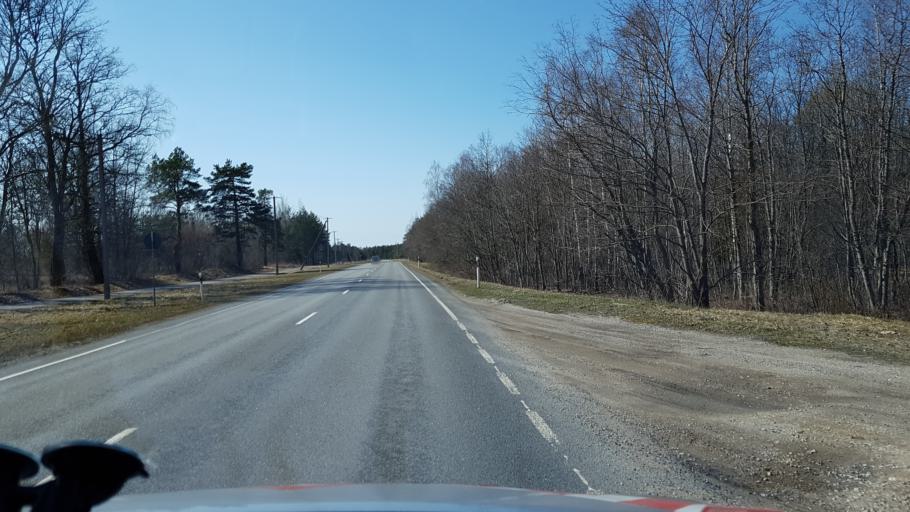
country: EE
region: Laeaene
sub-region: Haapsalu linn
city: Haapsalu
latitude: 58.9212
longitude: 23.5167
